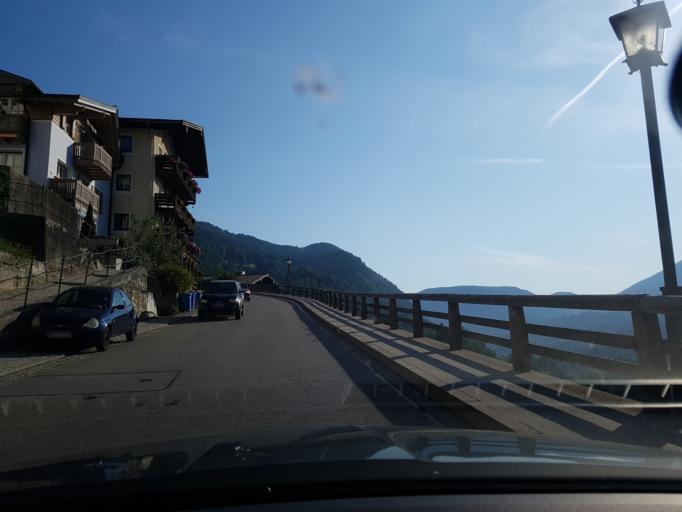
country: DE
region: Bavaria
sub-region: Upper Bavaria
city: Berchtesgaden
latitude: 47.6385
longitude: 13.0080
